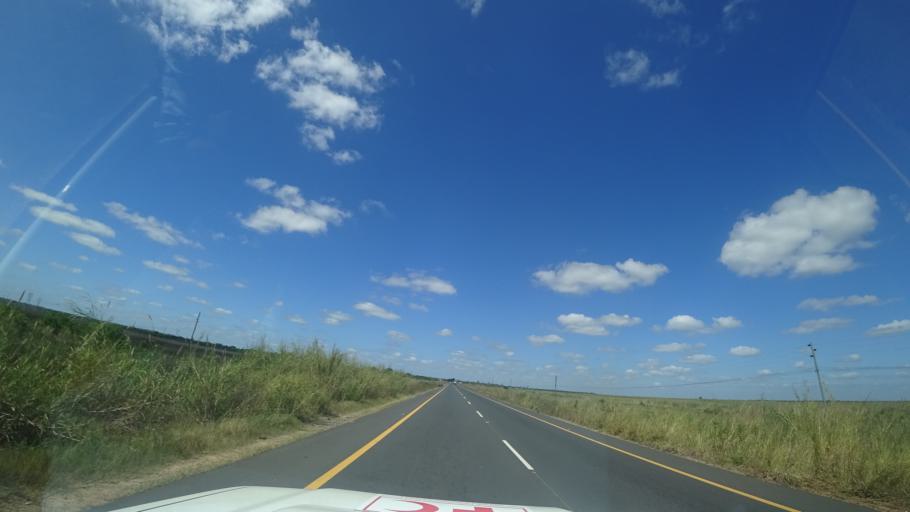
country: MZ
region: Sofala
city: Dondo
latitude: -19.4856
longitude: 34.5784
